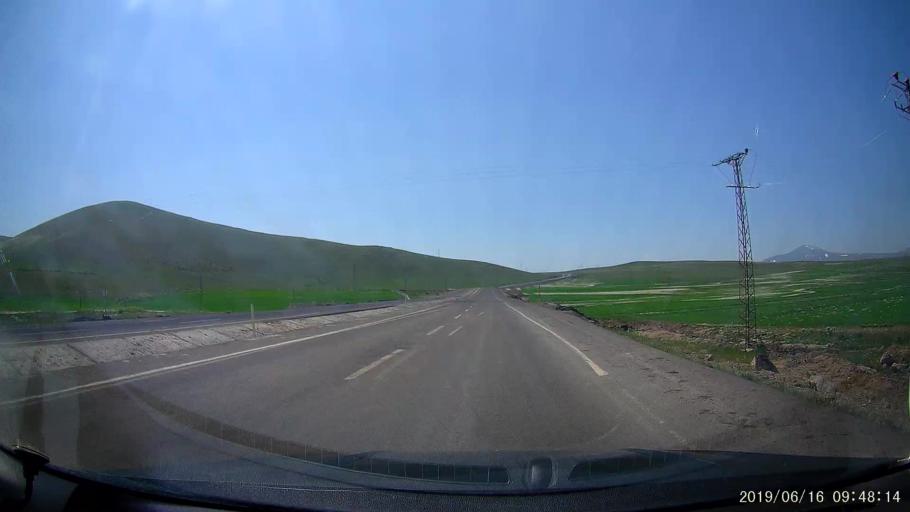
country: TR
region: Kars
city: Digor
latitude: 40.4356
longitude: 43.3511
